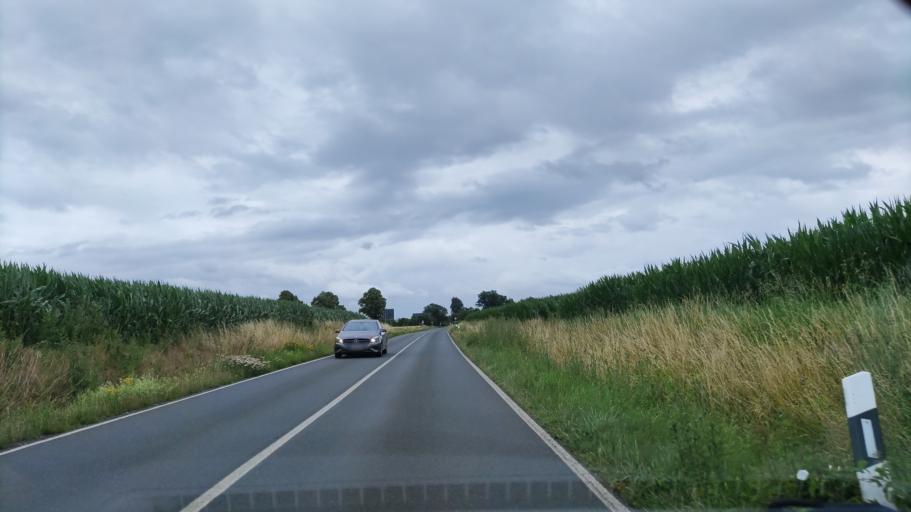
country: DE
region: North Rhine-Westphalia
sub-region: Regierungsbezirk Arnsberg
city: Soest
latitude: 51.5956
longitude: 8.0683
